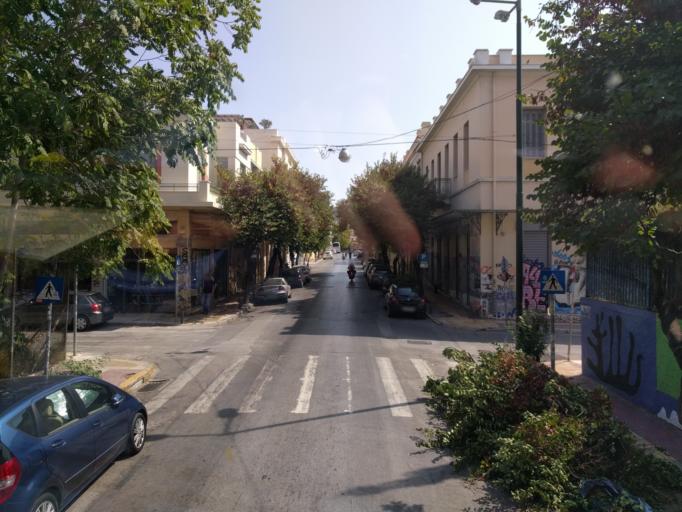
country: GR
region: Attica
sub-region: Nomarchia Athinas
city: Athens
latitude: 37.9796
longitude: 23.7197
